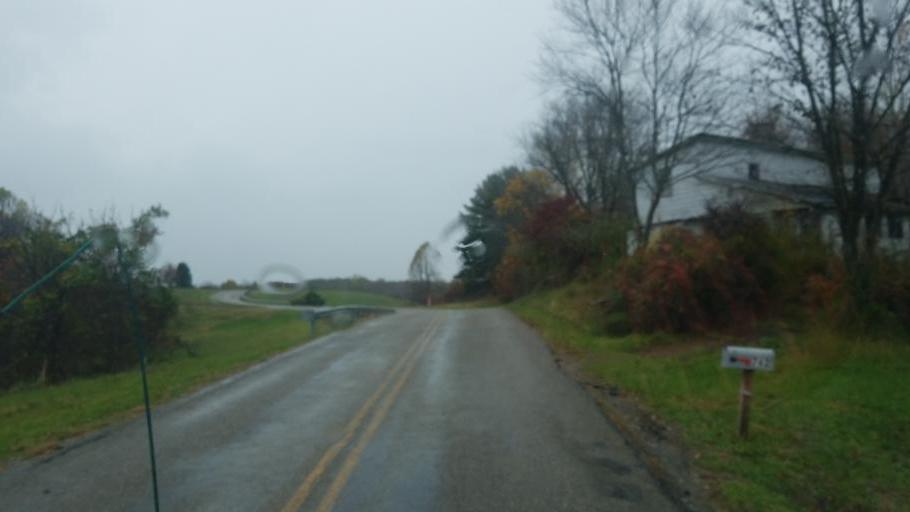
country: US
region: West Virginia
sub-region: Wood County
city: Vienna
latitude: 39.3450
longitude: -81.6269
